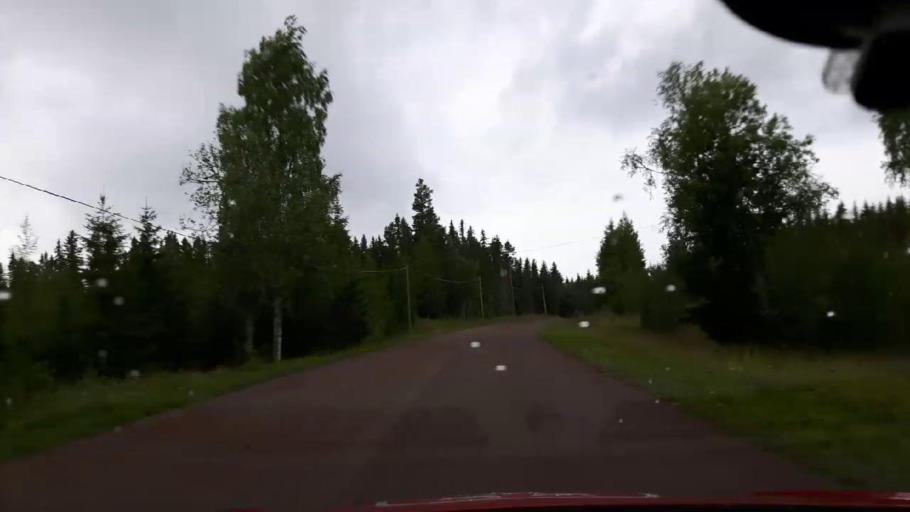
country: SE
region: Jaemtland
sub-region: Are Kommun
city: Jarpen
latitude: 63.3161
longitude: 13.6929
